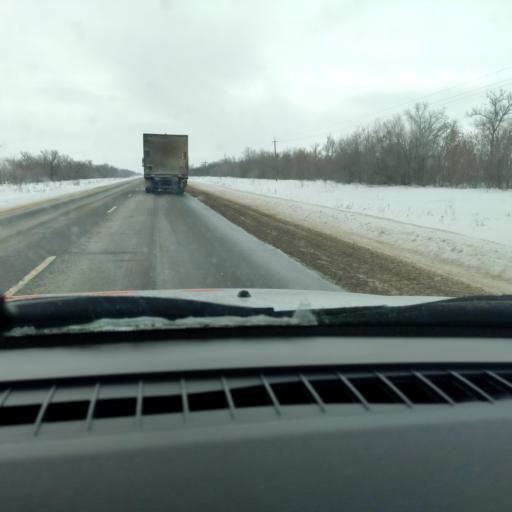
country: RU
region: Samara
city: Dubovyy Umet
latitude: 52.7772
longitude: 50.4934
